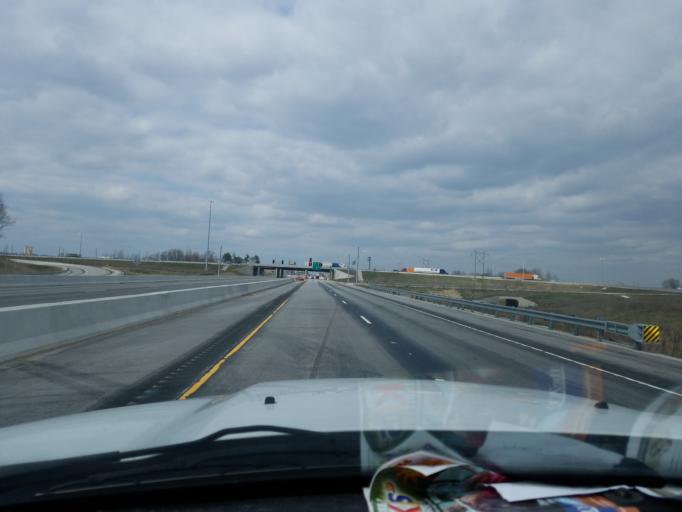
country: US
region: Indiana
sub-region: Vigo County
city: Terre Haute
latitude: 39.4277
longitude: -87.3329
